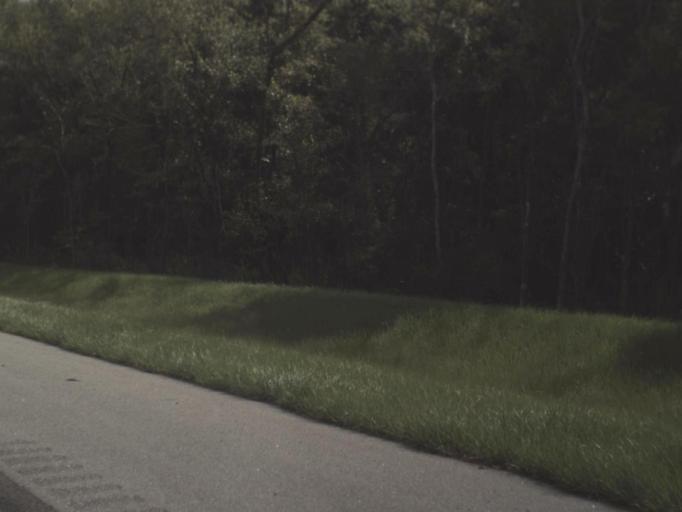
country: US
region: Florida
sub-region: Hillsborough County
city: Lutz
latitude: 28.1285
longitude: -82.4165
